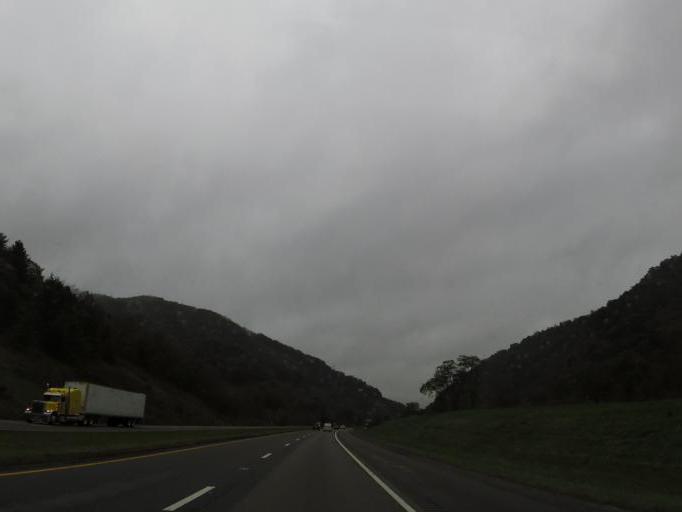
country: US
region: Virginia
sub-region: Wythe County
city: Wytheville
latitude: 36.9983
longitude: -81.0854
